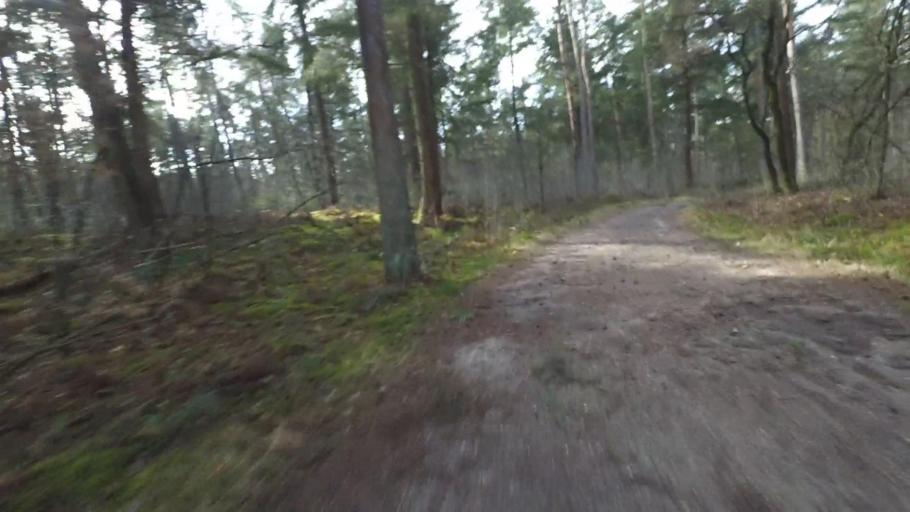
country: NL
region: Utrecht
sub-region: Gemeente Utrechtse Heuvelrug
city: Driebergen-Rijsenburg
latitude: 52.0628
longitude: 5.3177
